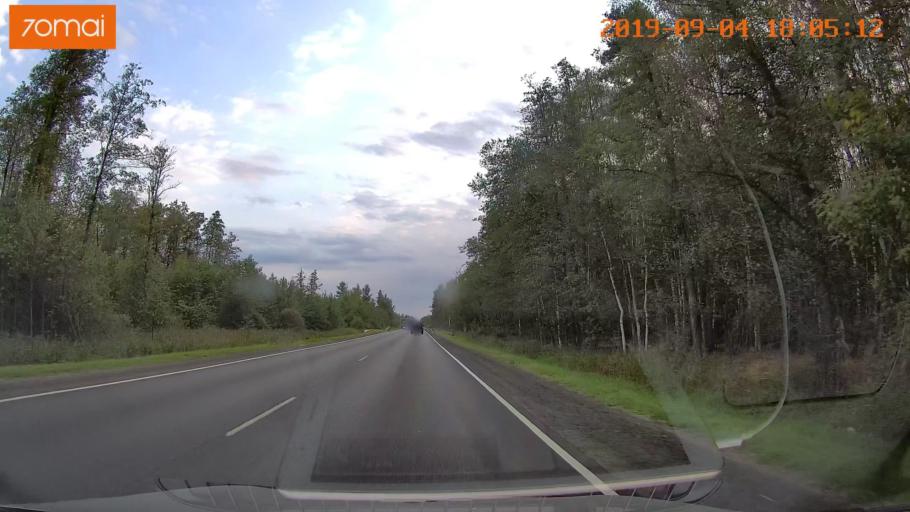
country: RU
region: Moskovskaya
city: Il'inskiy Pogost
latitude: 55.4440
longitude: 38.8295
